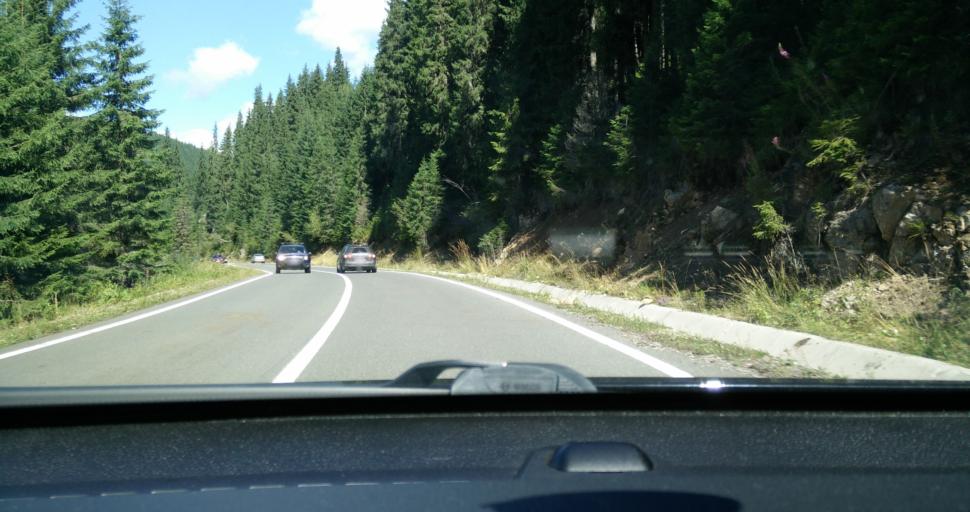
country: RO
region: Alba
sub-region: Comuna Sugag
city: Sugag
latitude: 45.5298
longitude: 23.6455
